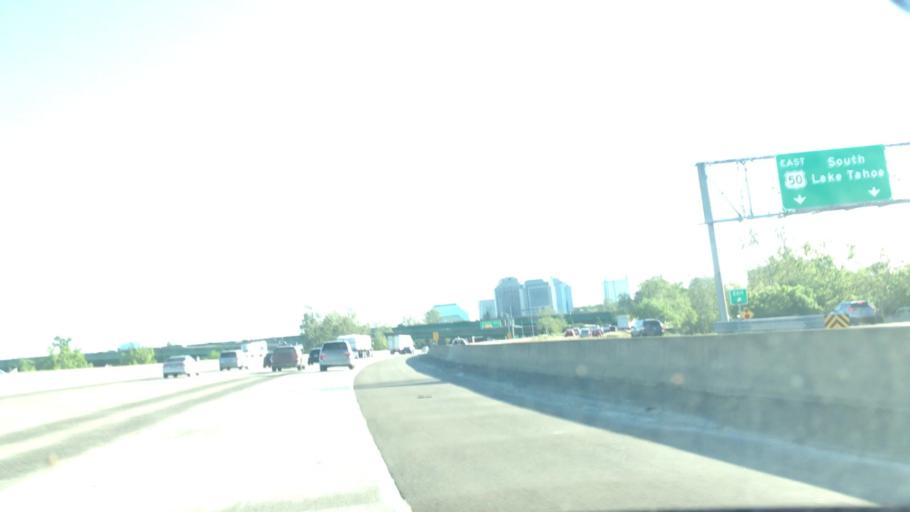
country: US
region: California
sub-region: Yolo County
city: West Sacramento
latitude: 38.5648
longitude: -121.5139
